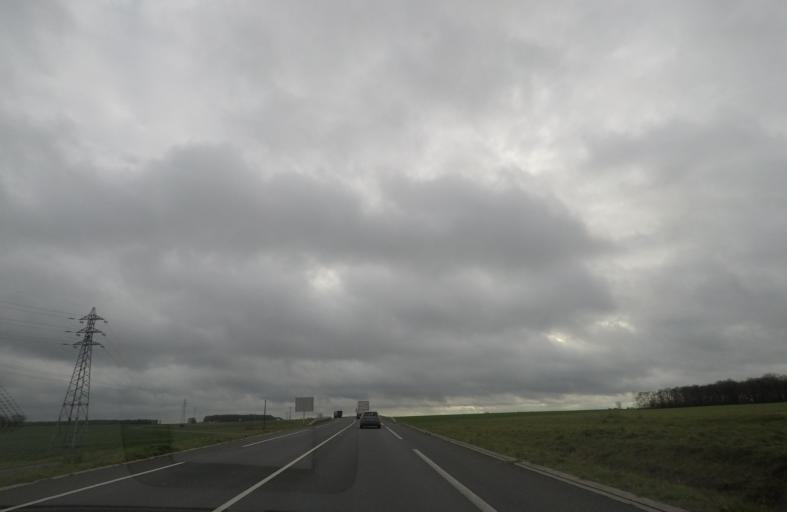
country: FR
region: Centre
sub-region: Departement du Loir-et-Cher
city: Vendome
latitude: 47.7703
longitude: 1.0621
